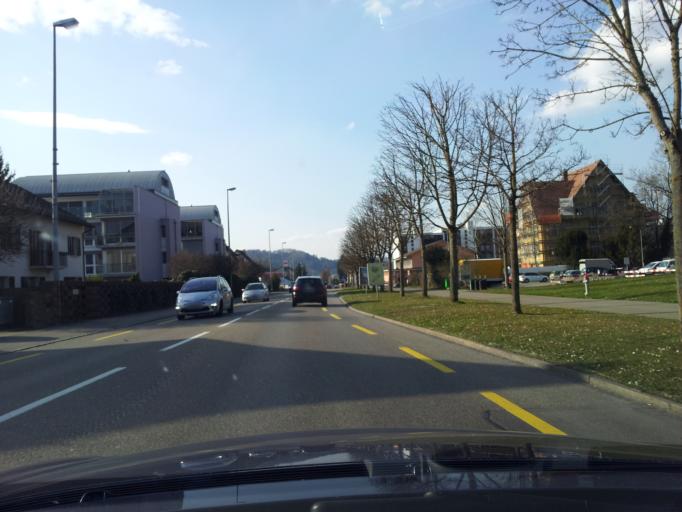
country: CH
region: Aargau
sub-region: Bezirk Baden
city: Neuenhof
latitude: 47.4505
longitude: 8.3261
